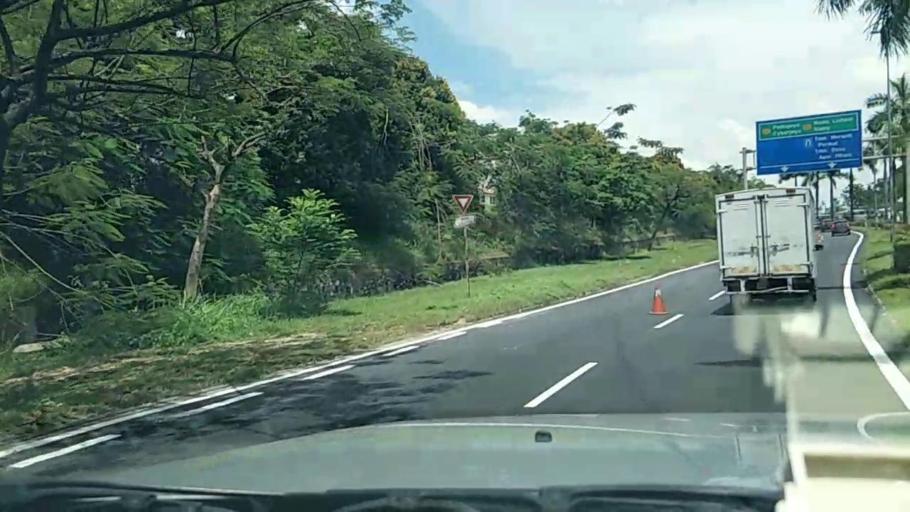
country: MY
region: Selangor
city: Subang Jaya
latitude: 2.9676
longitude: 101.6142
